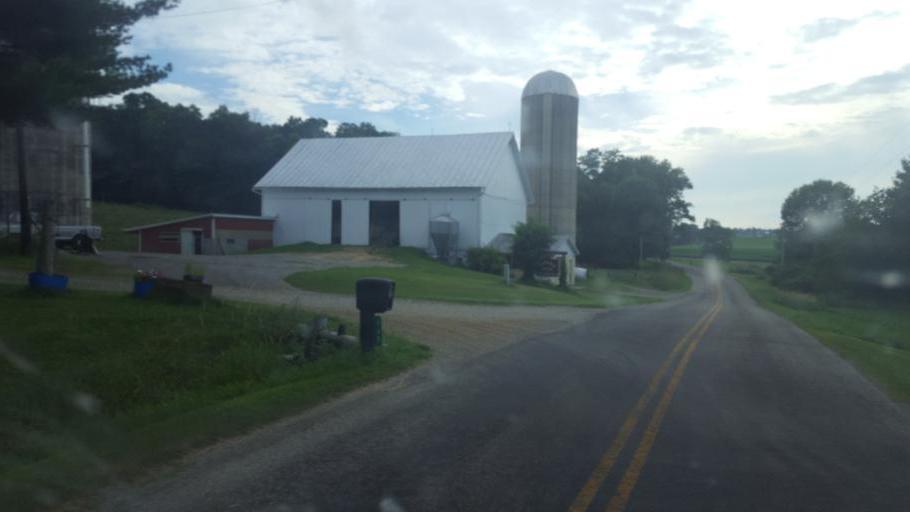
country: US
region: Ohio
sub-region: Ashland County
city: Loudonville
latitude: 40.7723
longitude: -82.2153
